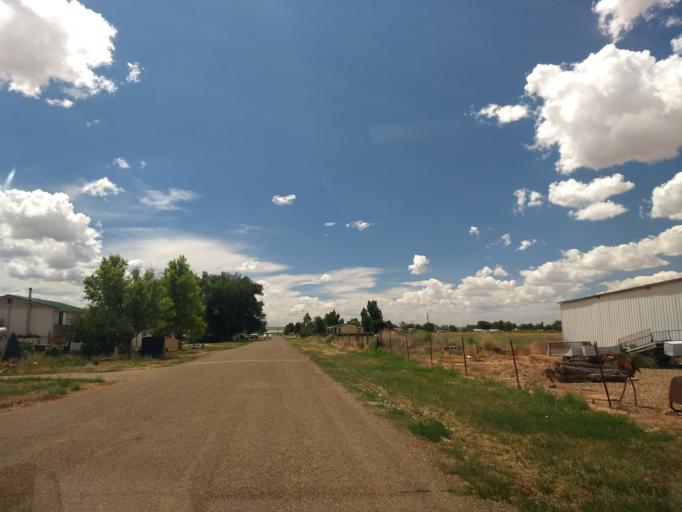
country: US
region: Arizona
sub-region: Coconino County
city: Fredonia
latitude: 36.9451
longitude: -112.5206
